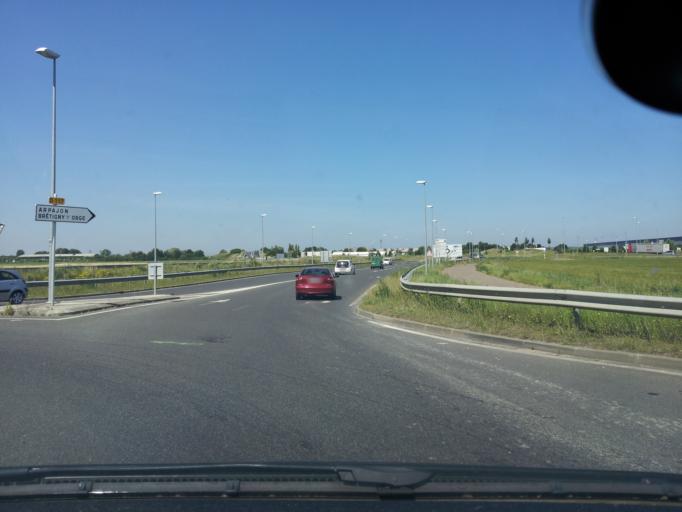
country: FR
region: Ile-de-France
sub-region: Departement de l'Essonne
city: Marolles-en-Hurepoix
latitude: 48.5775
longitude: 2.3018
